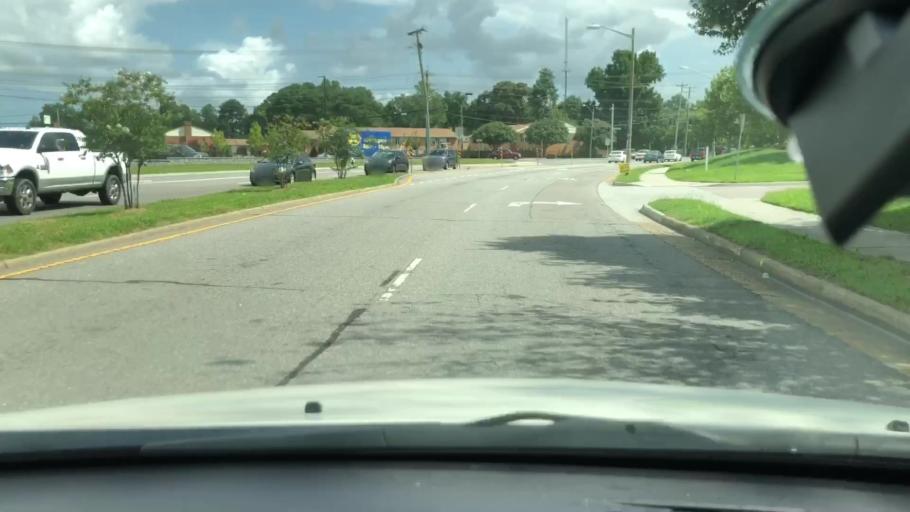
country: US
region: Virginia
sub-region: City of Chesapeake
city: Chesapeake
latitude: 36.8117
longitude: -76.2071
